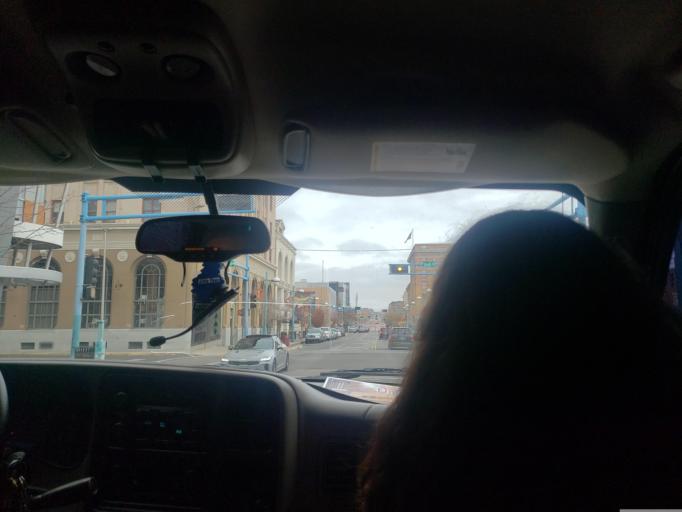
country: US
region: New Mexico
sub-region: Bernalillo County
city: Albuquerque
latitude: 35.0847
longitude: -106.6511
